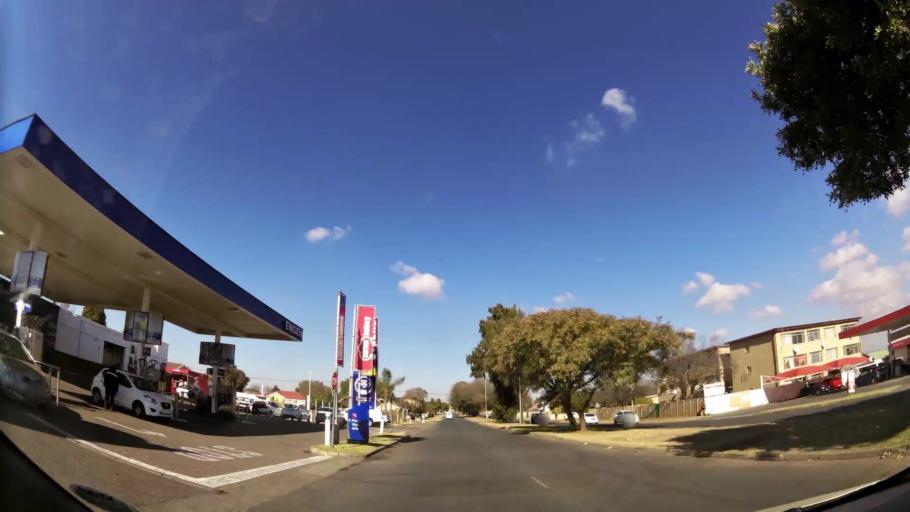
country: ZA
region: Gauteng
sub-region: City of Johannesburg Metropolitan Municipality
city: Roodepoort
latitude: -26.1343
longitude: 27.8347
